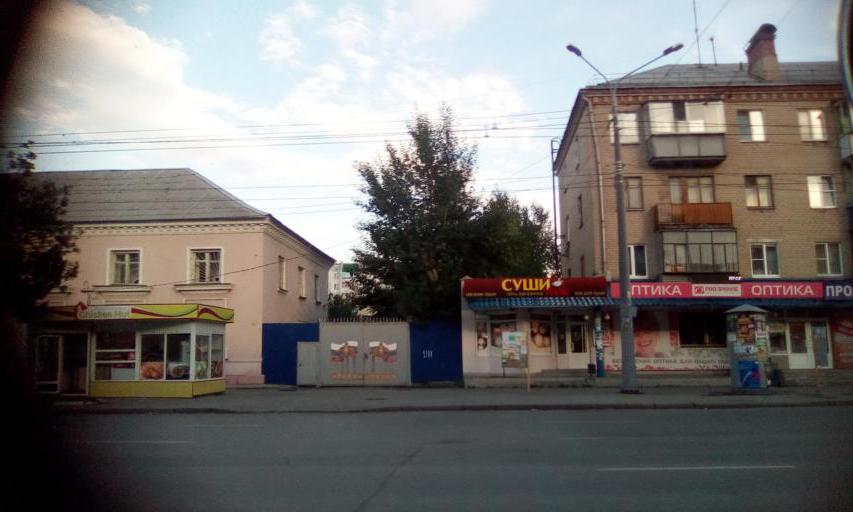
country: RU
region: Chelyabinsk
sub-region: Gorod Chelyabinsk
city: Chelyabinsk
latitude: 55.1420
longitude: 61.3763
